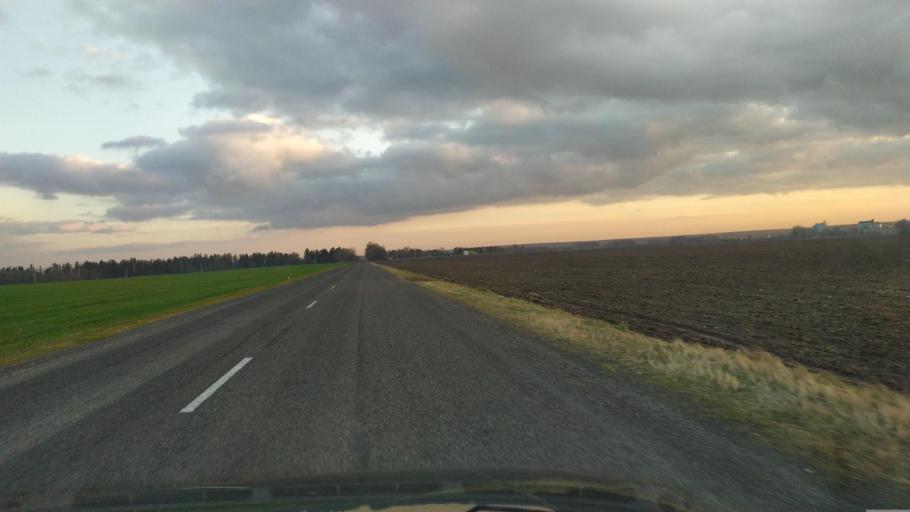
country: BY
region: Brest
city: Kamyanyets
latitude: 52.4192
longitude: 23.7786
